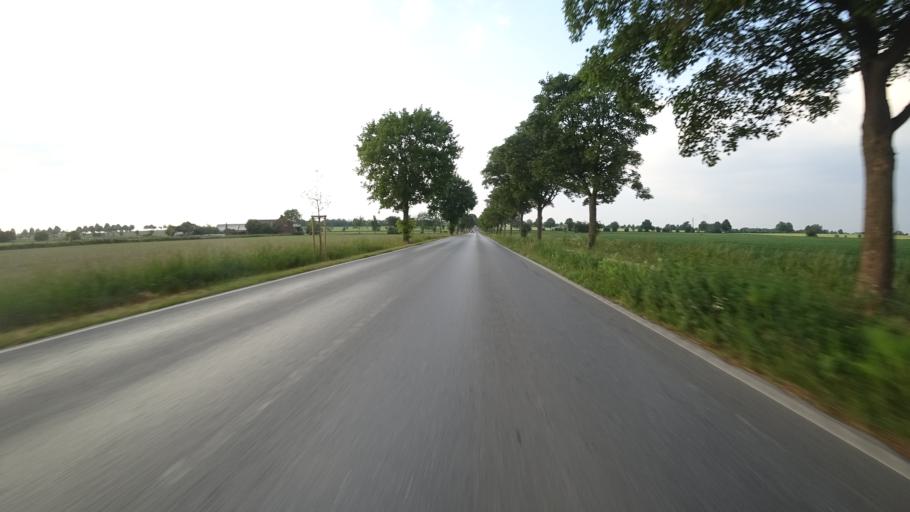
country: DE
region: North Rhine-Westphalia
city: Erwitte
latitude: 51.6397
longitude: 8.3572
